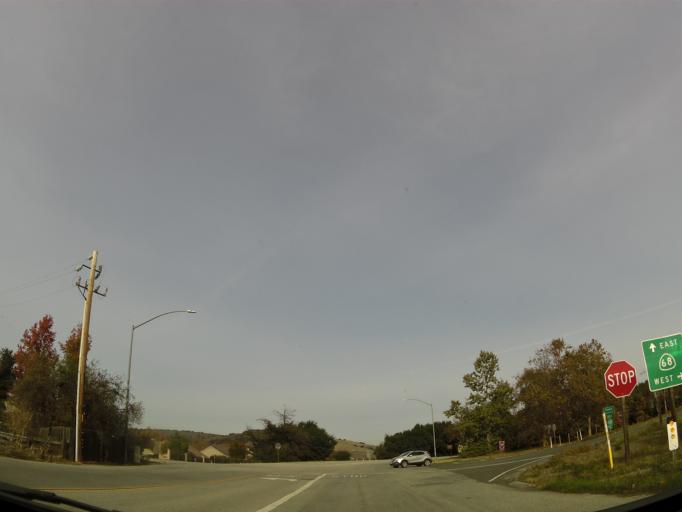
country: US
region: California
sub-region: Monterey County
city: Salinas
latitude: 36.6063
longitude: -121.6948
